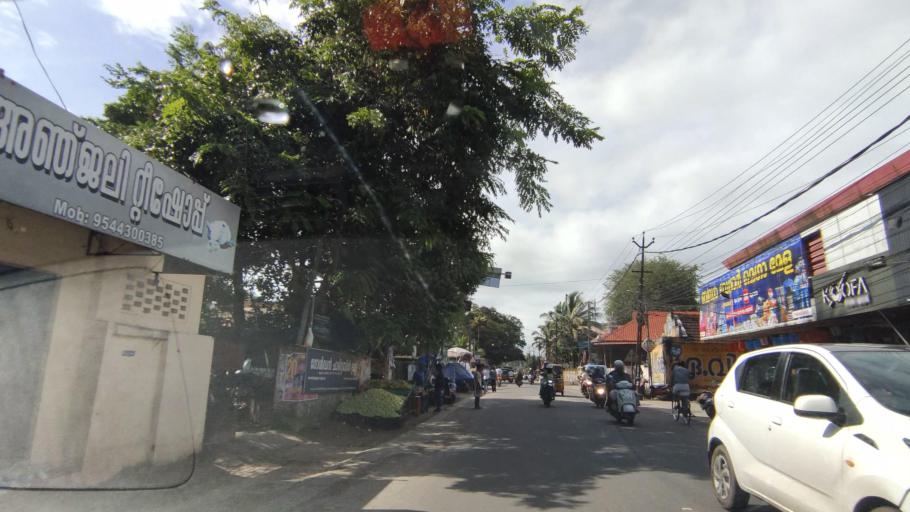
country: IN
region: Kerala
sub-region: Alappuzha
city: Alleppey
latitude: 9.5062
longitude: 76.3403
